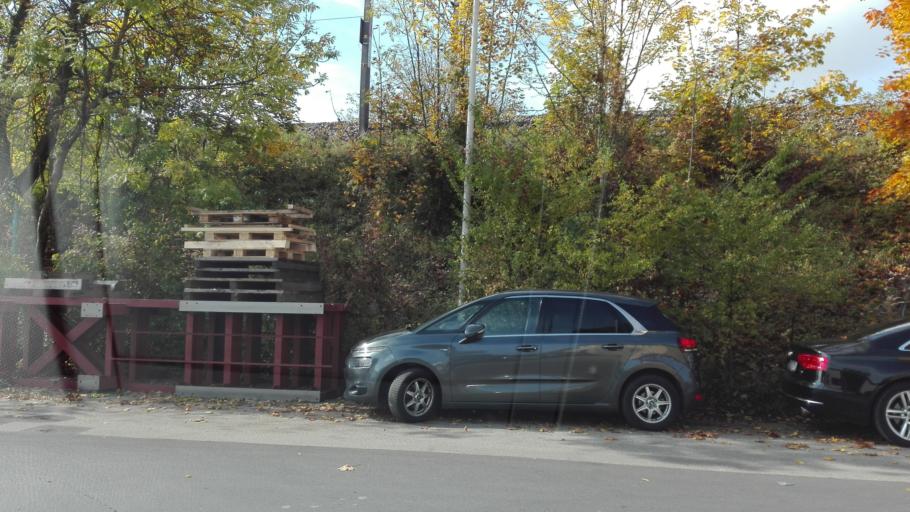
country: AT
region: Upper Austria
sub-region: Politischer Bezirk Linz-Land
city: Leonding
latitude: 48.2574
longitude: 14.2767
